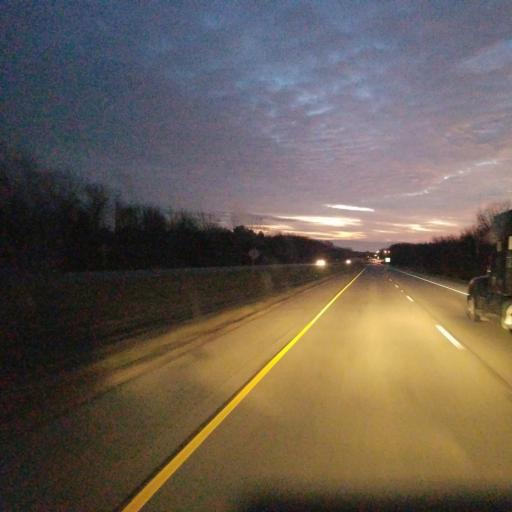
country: US
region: Illinois
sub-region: Peoria County
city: Bellevue
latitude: 40.6939
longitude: -89.6902
